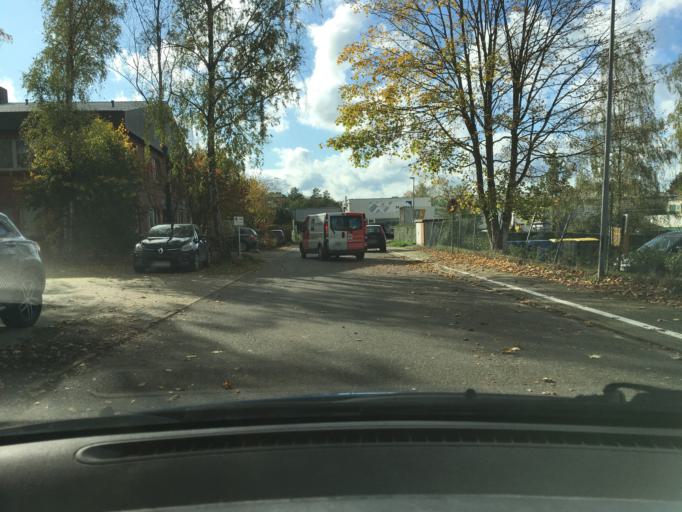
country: DE
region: Lower Saxony
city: Buchholz in der Nordheide
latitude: 53.3471
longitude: 9.8655
